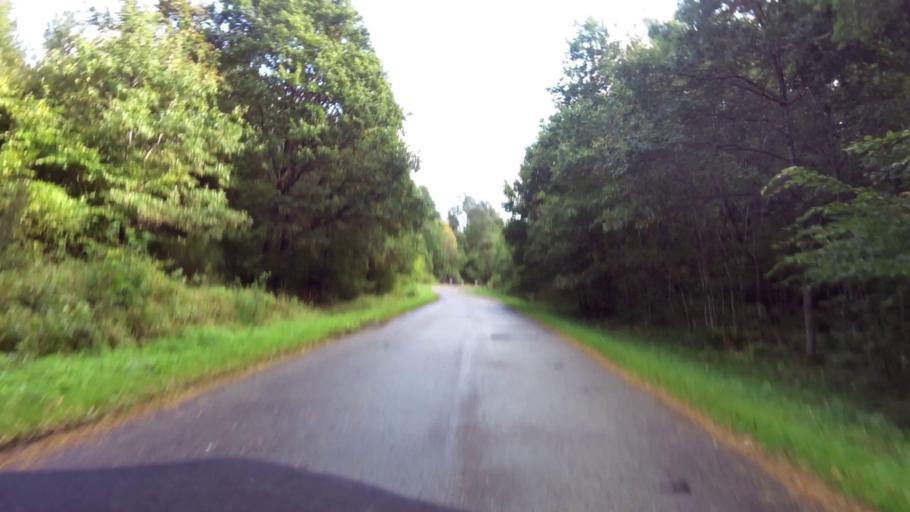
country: PL
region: West Pomeranian Voivodeship
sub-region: Powiat bialogardzki
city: Bialogard
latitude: 53.9928
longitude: 16.1018
